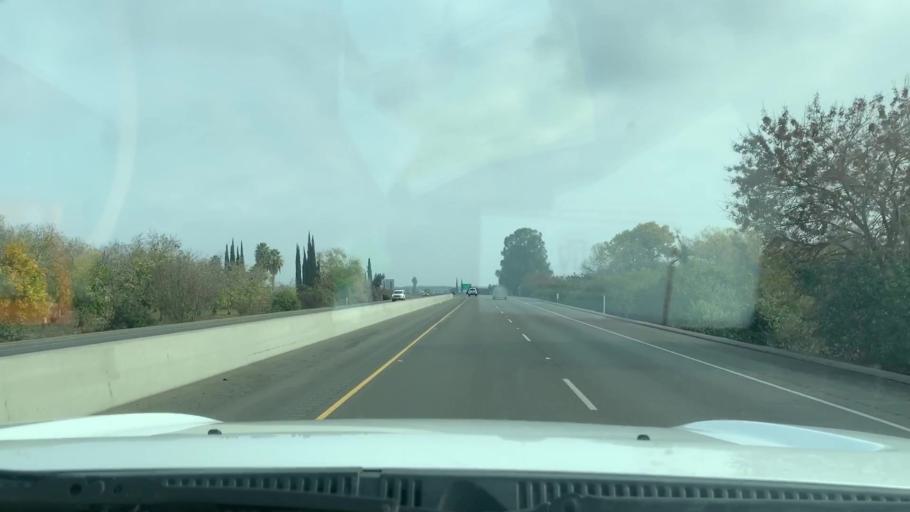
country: US
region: California
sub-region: Kings County
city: Lemoore
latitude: 36.2916
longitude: -119.7733
